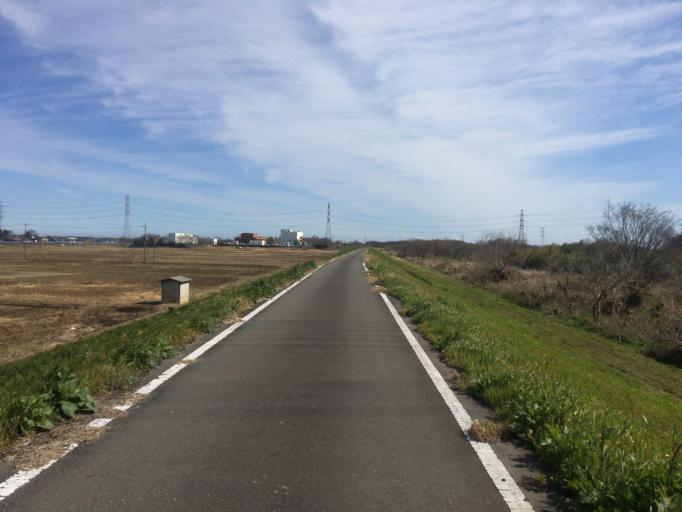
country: JP
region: Saitama
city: Sakado
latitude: 35.9900
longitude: 139.4085
